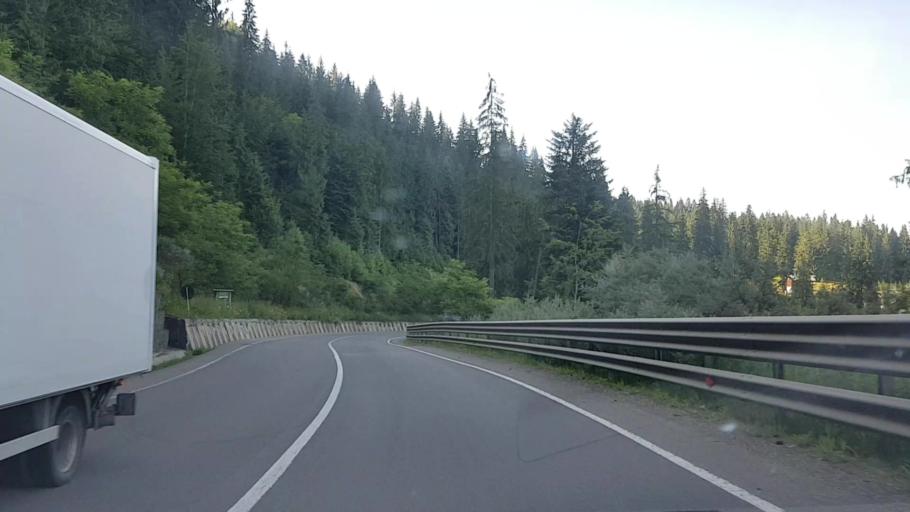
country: RO
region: Bistrita-Nasaud
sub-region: Comuna Lunca Ilvei
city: Lunca Ilvei
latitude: 47.2296
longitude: 24.9634
